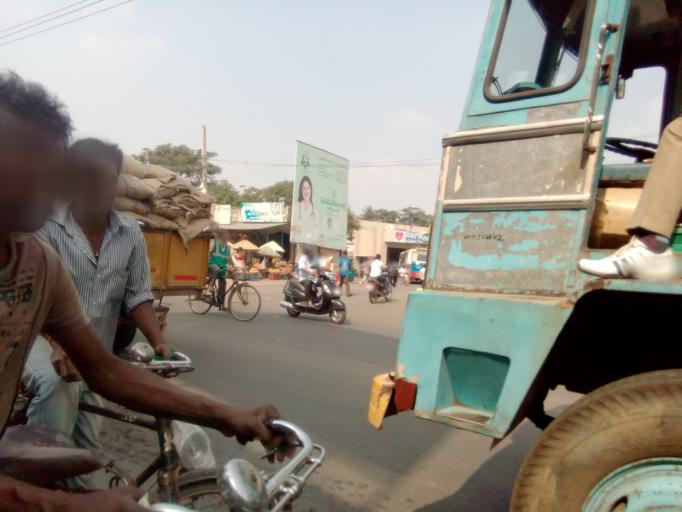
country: IN
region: Andhra Pradesh
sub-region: Vizianagaram District
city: Vizianagaram
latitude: 18.1080
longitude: 83.3994
